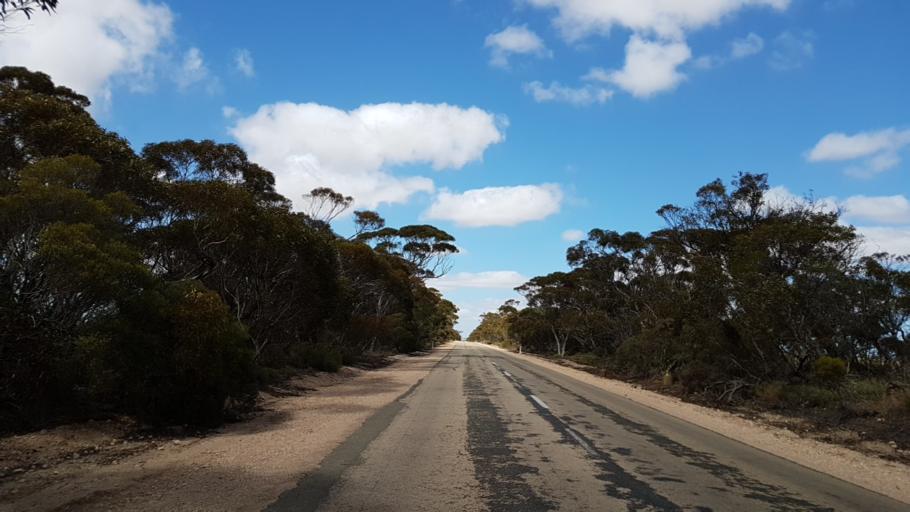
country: AU
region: South Australia
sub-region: Yorke Peninsula
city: Ardrossan
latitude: -34.5698
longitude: 137.8268
